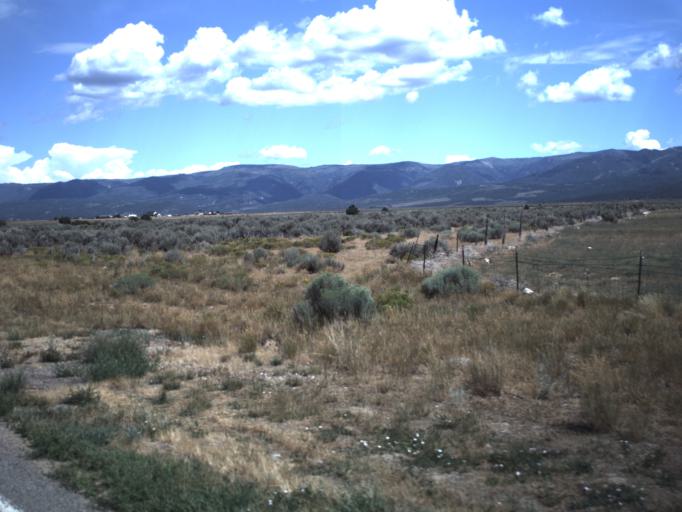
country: US
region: Utah
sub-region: Sanpete County
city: Mount Pleasant
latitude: 39.5100
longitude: -111.4815
